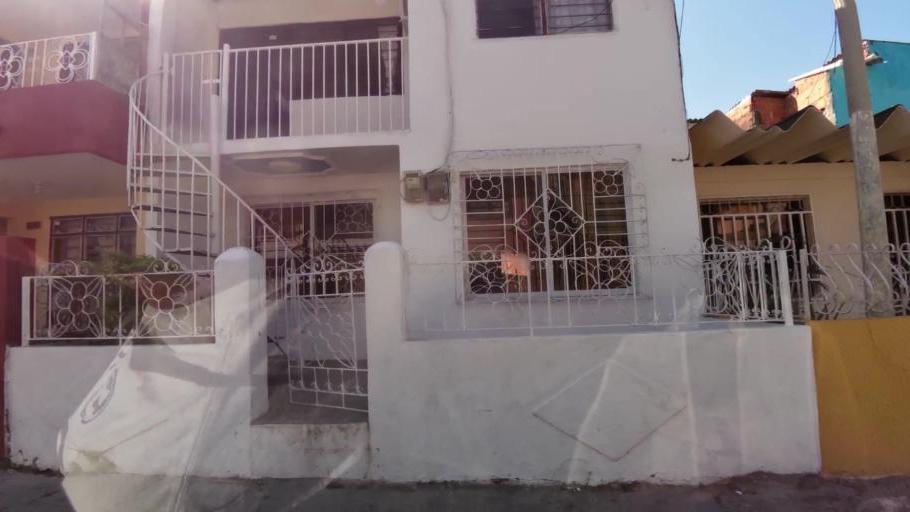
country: CO
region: Bolivar
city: Cartagena
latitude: 10.3944
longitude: -75.5138
